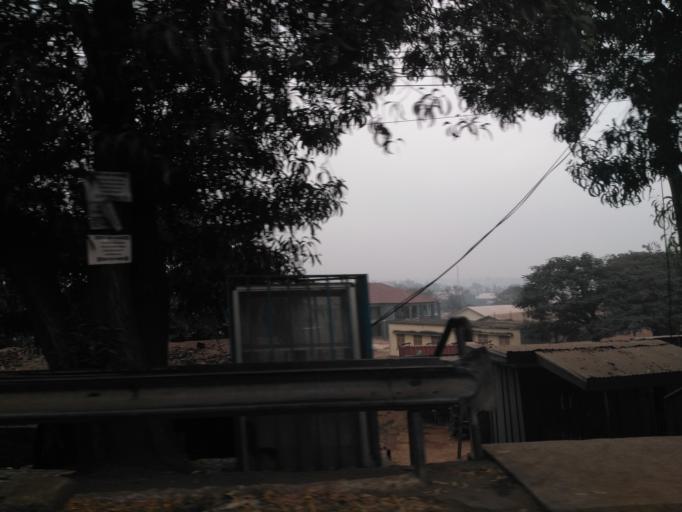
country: GH
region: Ashanti
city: Tafo
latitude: 6.7141
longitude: -1.6099
